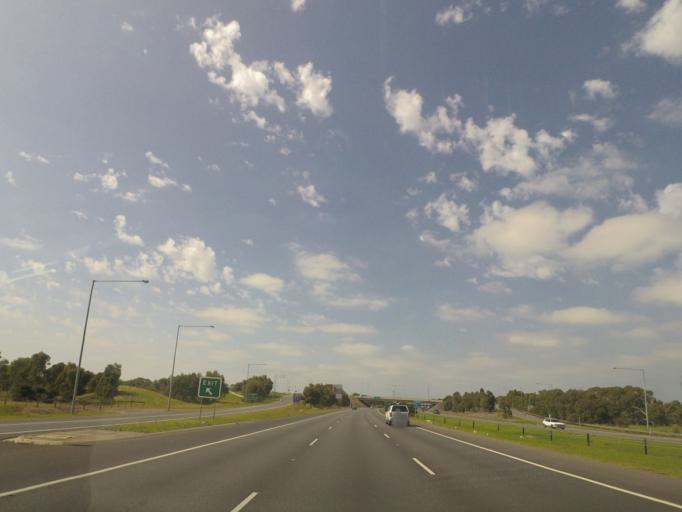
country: AU
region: Victoria
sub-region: Greater Dandenong
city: Dandenong
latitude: -37.9980
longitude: 145.1918
